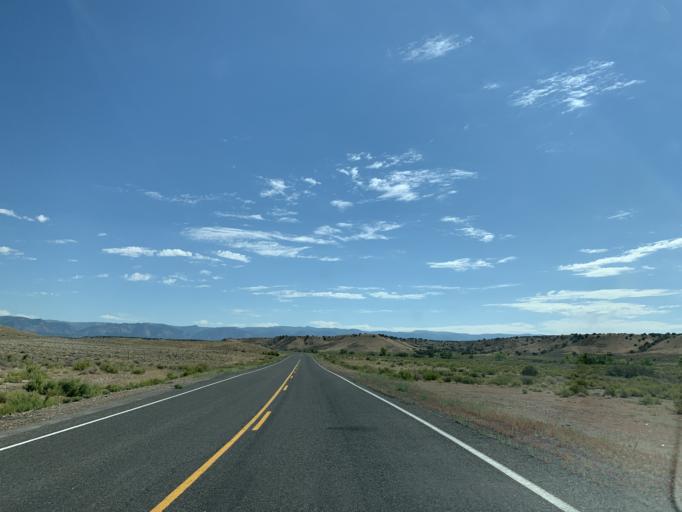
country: US
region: Utah
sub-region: Carbon County
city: Wellington
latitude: 39.5598
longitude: -110.6615
